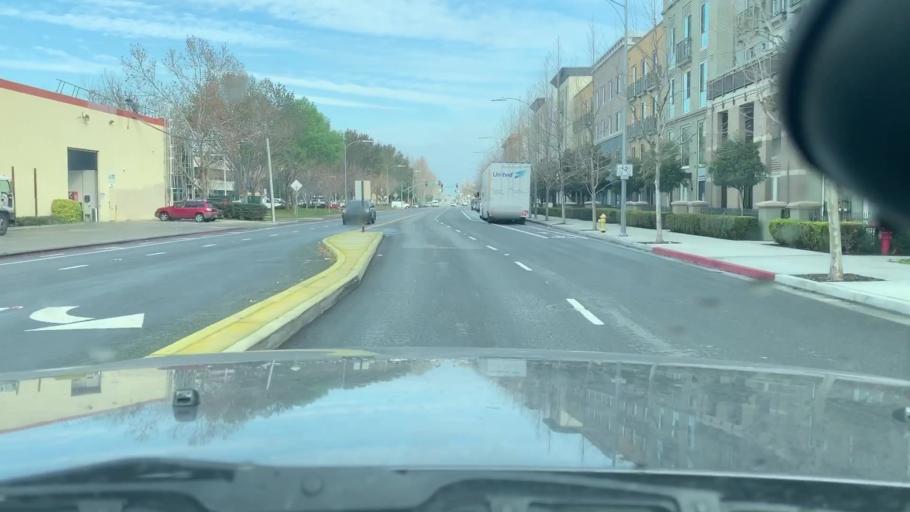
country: US
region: California
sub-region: Santa Clara County
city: Buena Vista
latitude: 37.3176
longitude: -121.9109
